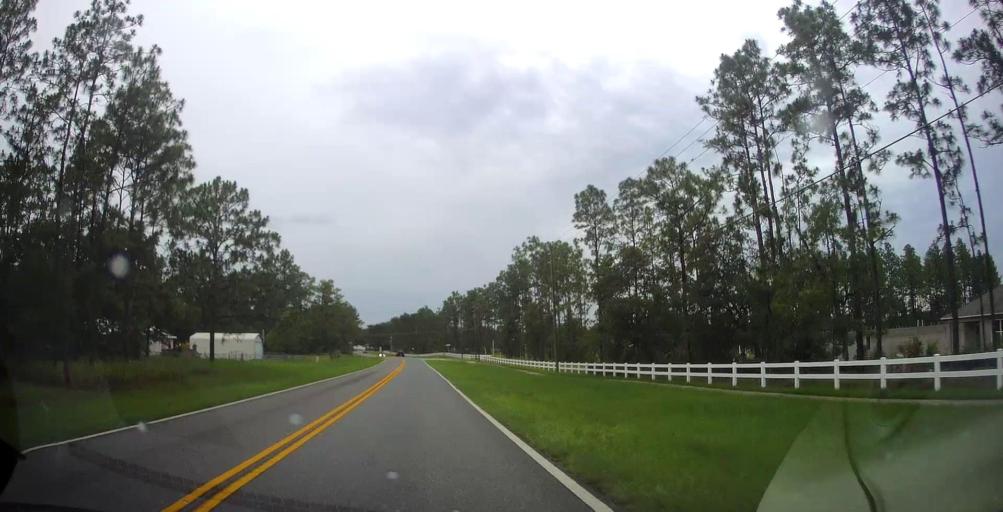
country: US
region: Florida
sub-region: Marion County
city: Silver Springs Shores
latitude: 29.1304
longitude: -82.0222
